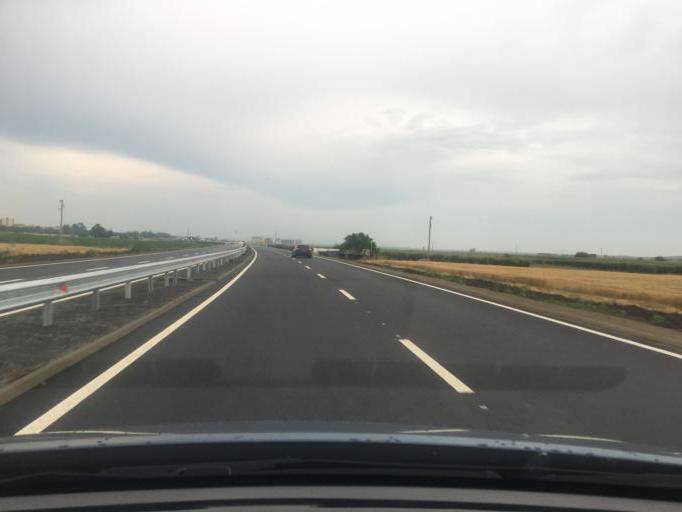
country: BG
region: Burgas
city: Aheloy
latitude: 42.6508
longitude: 27.6372
